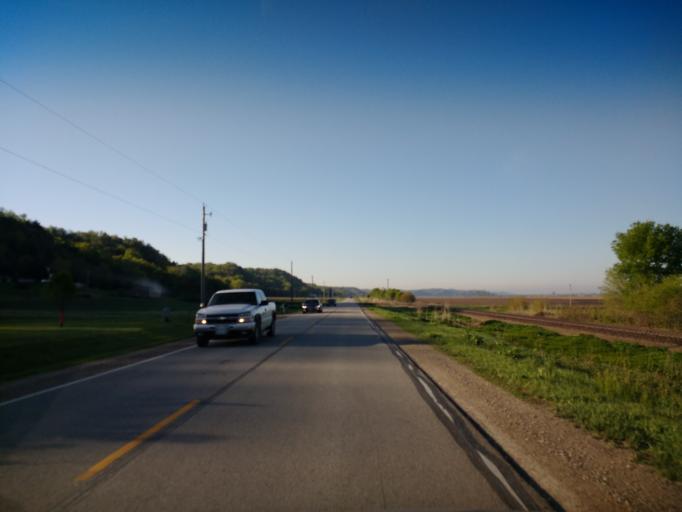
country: US
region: Iowa
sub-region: Harrison County
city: Missouri Valley
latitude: 41.4707
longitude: -95.8803
